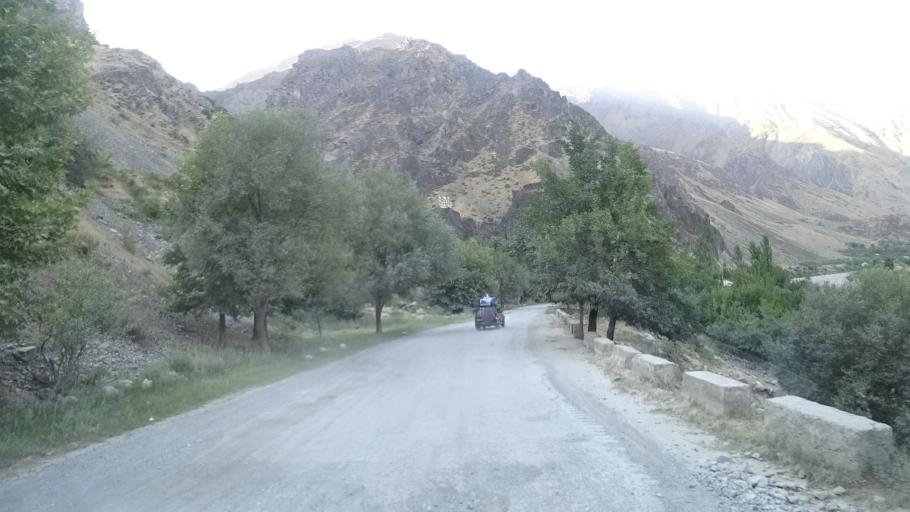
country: TJ
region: Gorno-Badakhshan
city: Qalaikhumb
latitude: 38.4013
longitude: 70.6721
